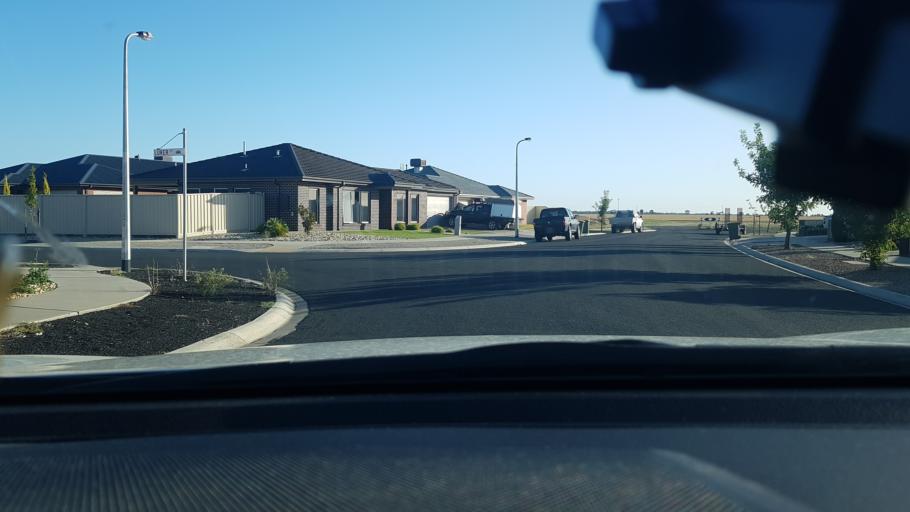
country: AU
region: Victoria
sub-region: Horsham
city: Horsham
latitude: -36.7144
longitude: 142.1759
